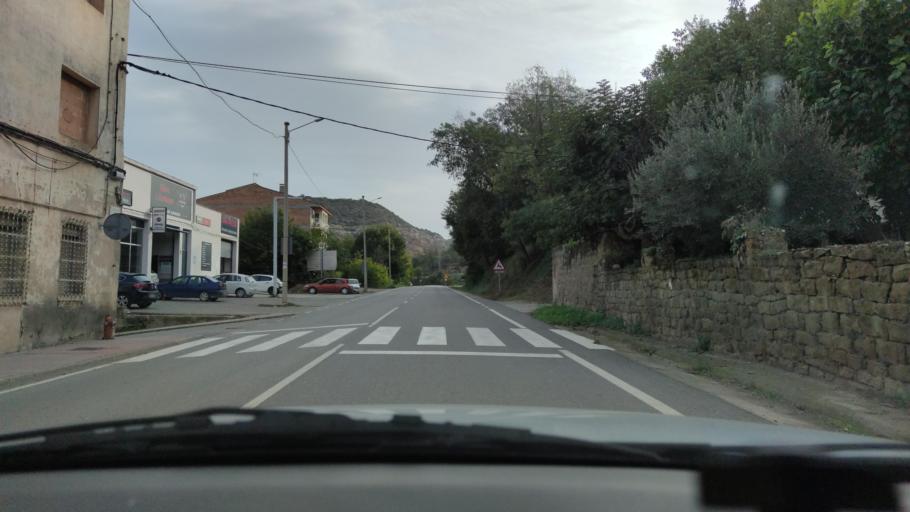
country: ES
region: Catalonia
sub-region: Provincia de Lleida
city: Artesa de Segre
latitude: 41.8963
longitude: 1.0543
